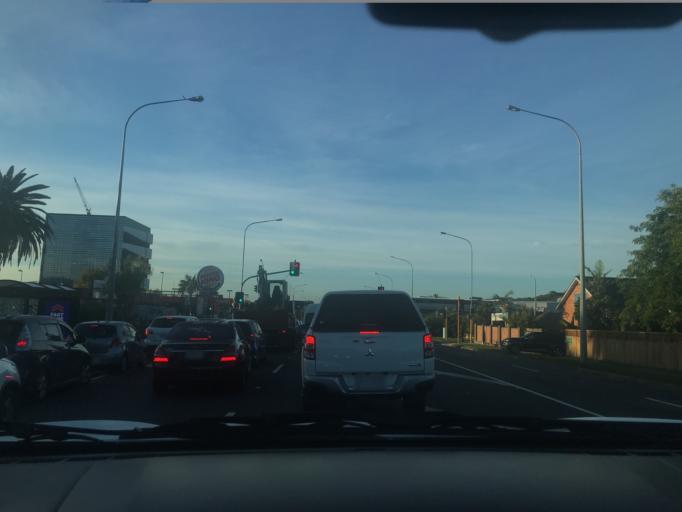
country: NZ
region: Auckland
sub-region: Auckland
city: Tamaki
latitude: -36.9128
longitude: 174.8384
